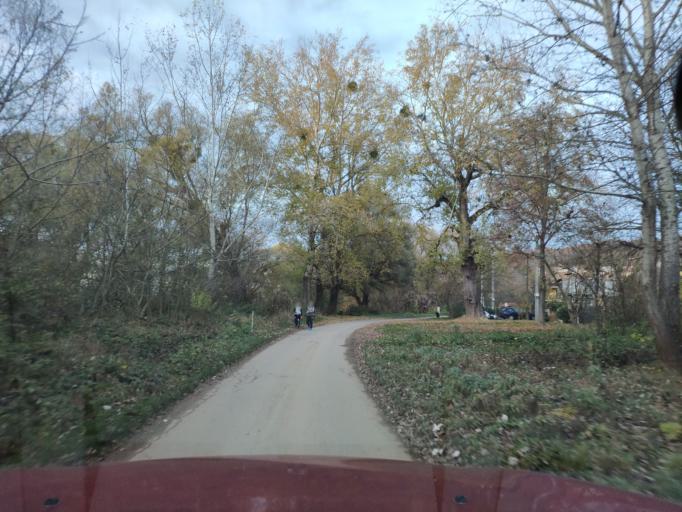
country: SK
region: Kosicky
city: Kosice
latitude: 48.6638
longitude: 21.3538
